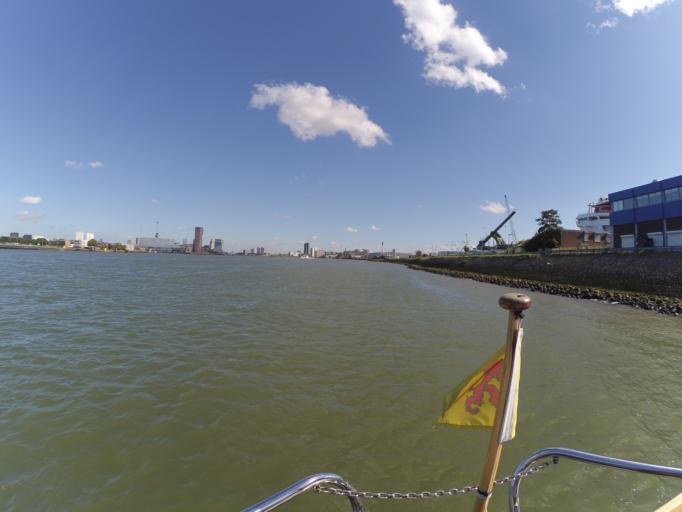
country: NL
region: South Holland
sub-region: Gemeente Rotterdam
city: Delfshaven
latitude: 51.8993
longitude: 4.4420
